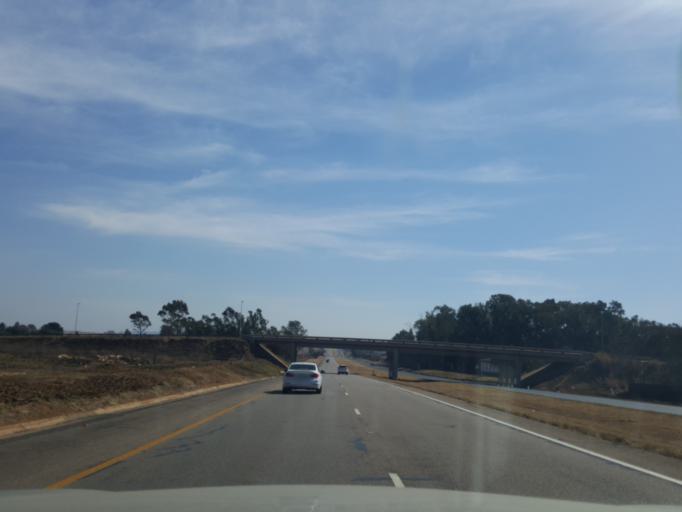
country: ZA
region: Gauteng
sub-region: City of Tshwane Metropolitan Municipality
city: Bronkhorstspruit
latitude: -25.8176
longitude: 28.7361
